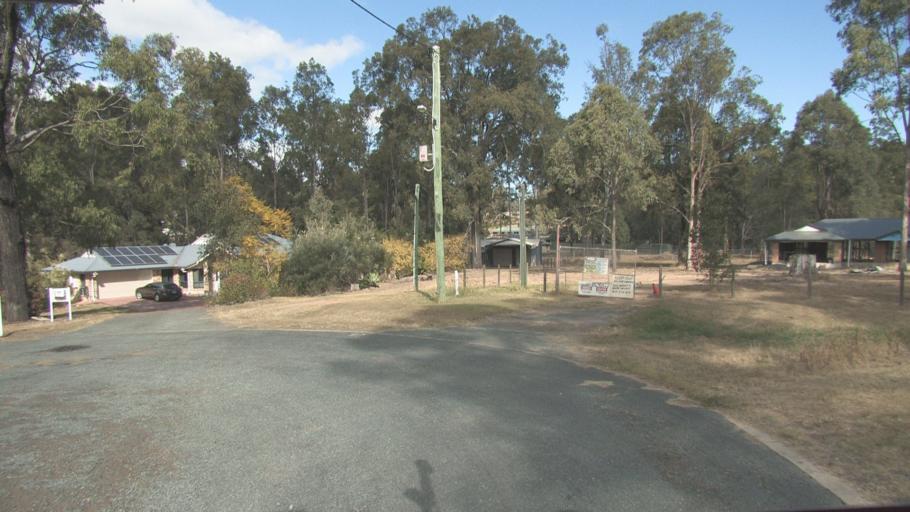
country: AU
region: Queensland
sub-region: Logan
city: Cedar Vale
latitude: -27.8773
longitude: 153.0045
